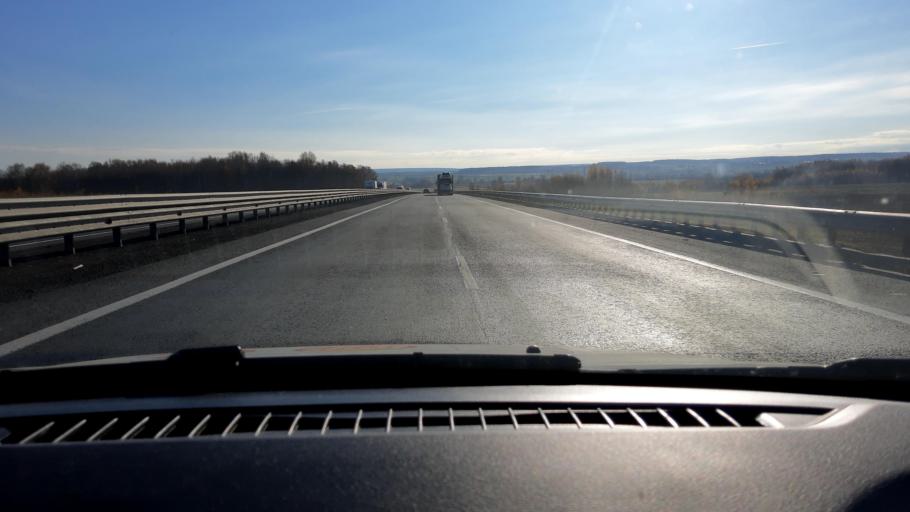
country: RU
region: Nizjnij Novgorod
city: Burevestnik
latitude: 56.1314
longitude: 43.7774
